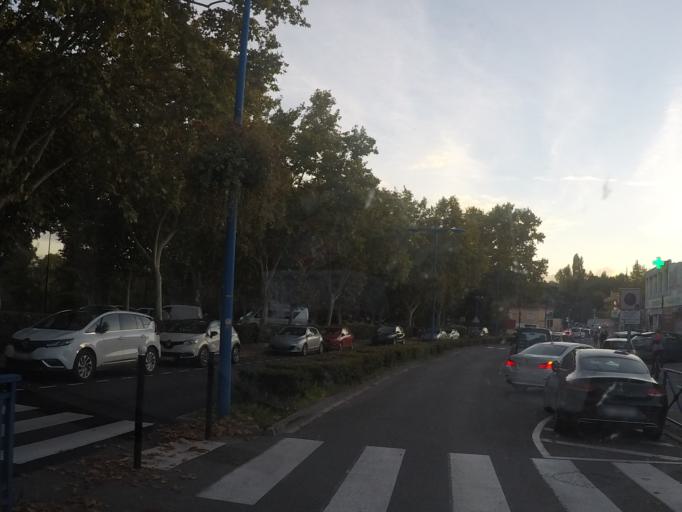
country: FR
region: Provence-Alpes-Cote d'Azur
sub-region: Departement des Alpes-de-Haute-Provence
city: Manosque
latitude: 43.8283
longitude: 5.7822
